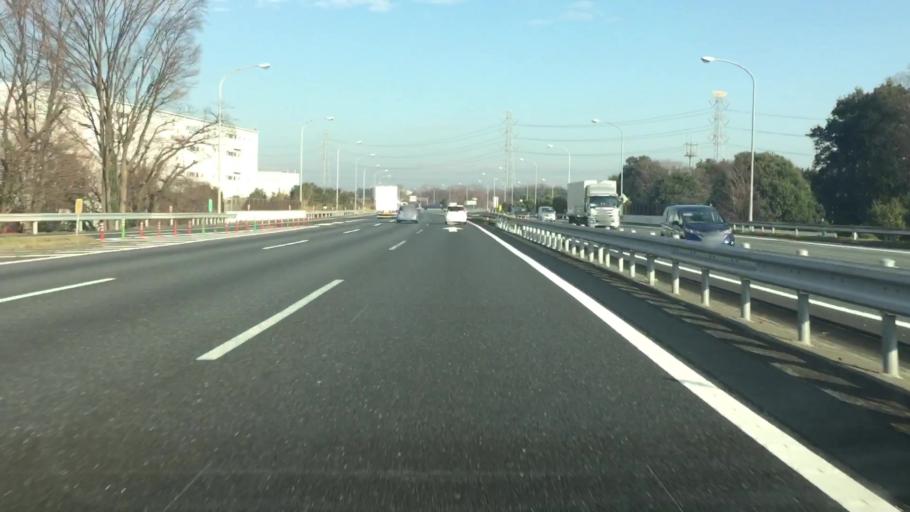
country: JP
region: Saitama
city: Sakado
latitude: 36.0266
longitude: 139.3816
